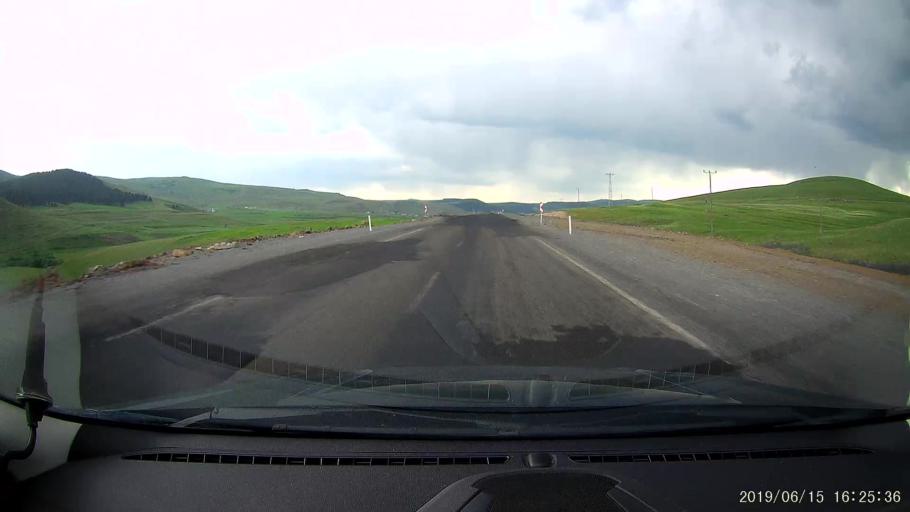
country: TR
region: Ardahan
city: Hanak
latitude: 41.1519
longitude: 42.8683
